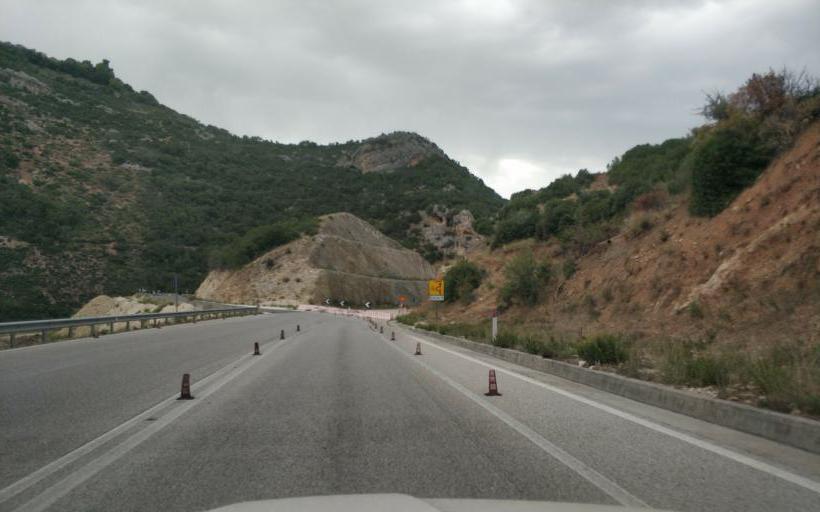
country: AL
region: Fier
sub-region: Rrethi i Mallakastres
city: Kute
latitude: 40.5090
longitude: 19.7548
